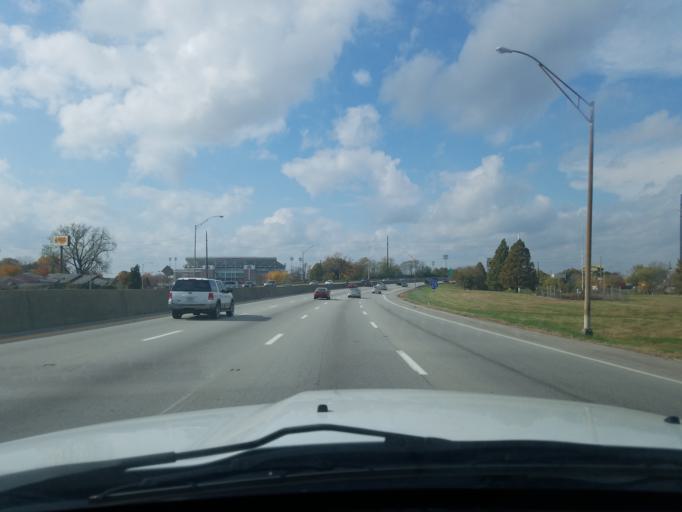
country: US
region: Kentucky
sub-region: Jefferson County
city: Audubon Park
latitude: 38.2067
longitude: -85.7480
